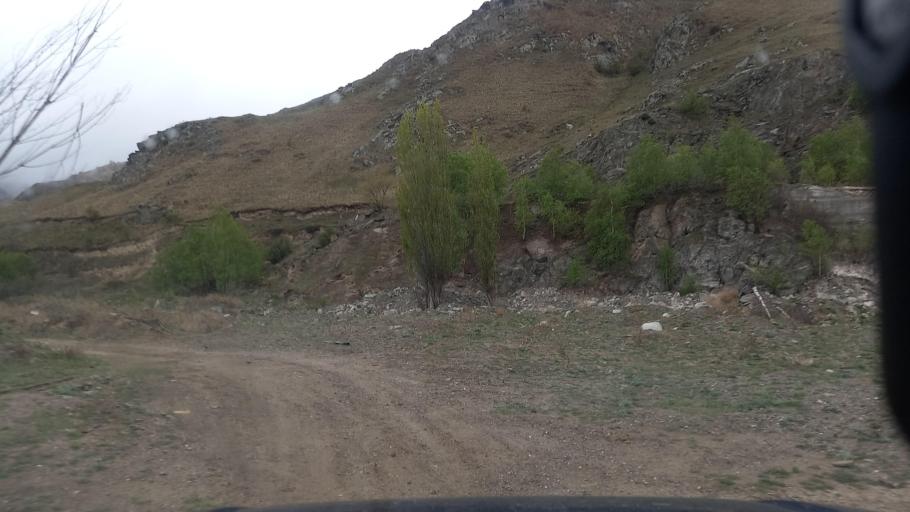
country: RU
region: Kabardino-Balkariya
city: Bylym
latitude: 43.4538
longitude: 43.0004
